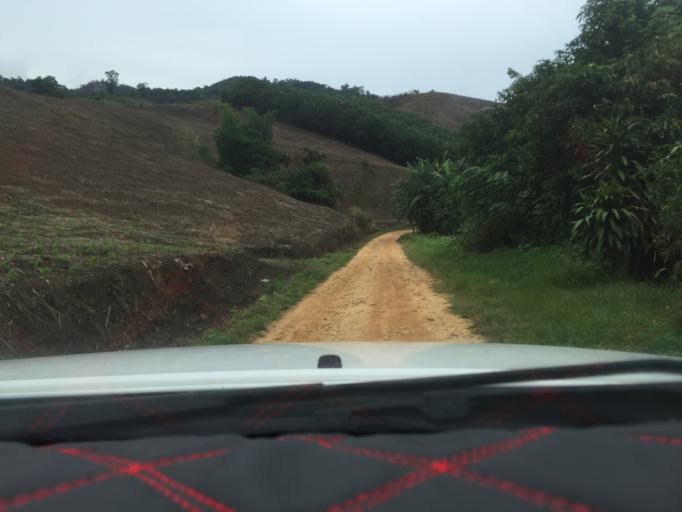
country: TH
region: Chiang Rai
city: Khun Tan
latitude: 19.7815
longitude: 100.4962
